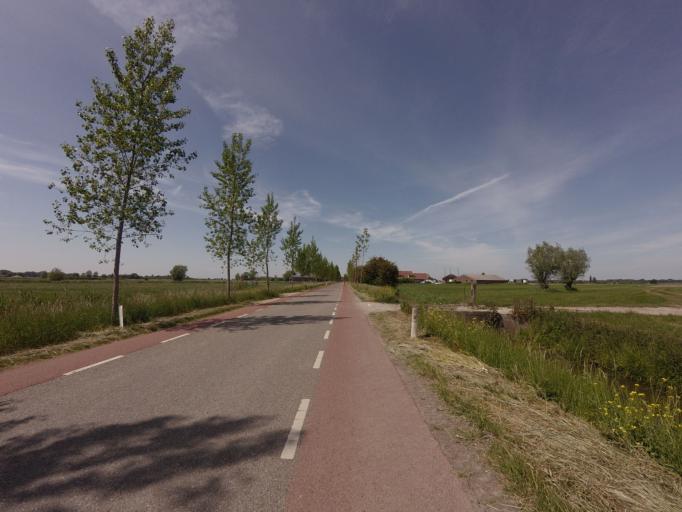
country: NL
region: Utrecht
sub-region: Gemeente IJsselstein
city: IJsselstein
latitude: 52.0524
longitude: 5.0316
